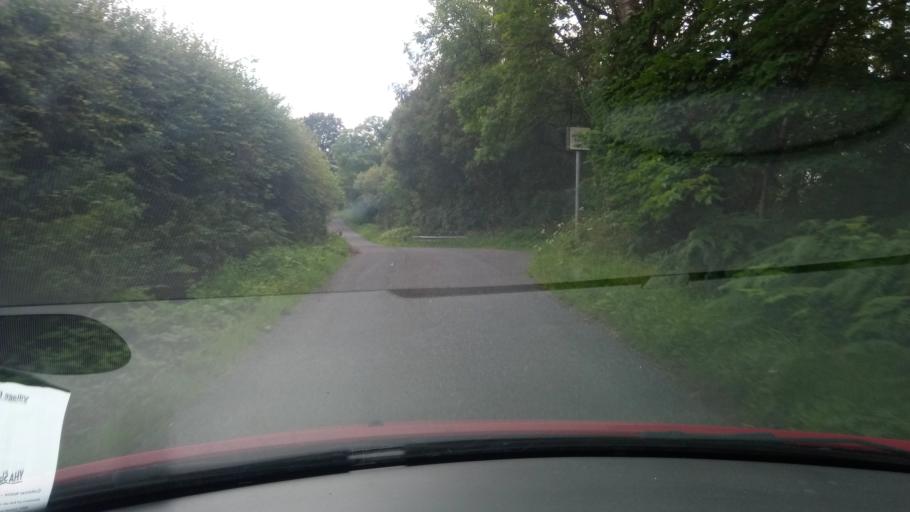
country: GB
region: Scotland
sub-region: The Scottish Borders
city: Jedburgh
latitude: 55.4078
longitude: -2.6455
